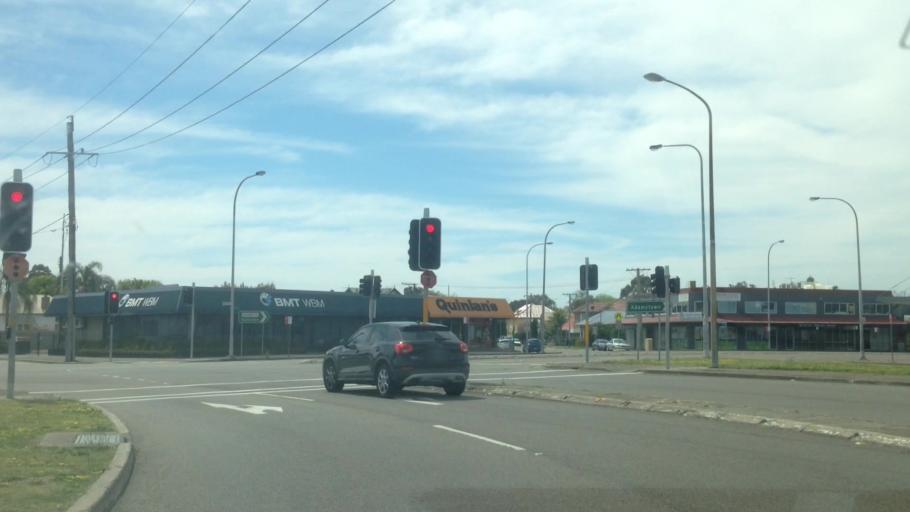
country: AU
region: New South Wales
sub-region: Newcastle
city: Broadmeadow
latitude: -32.9248
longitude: 151.7370
